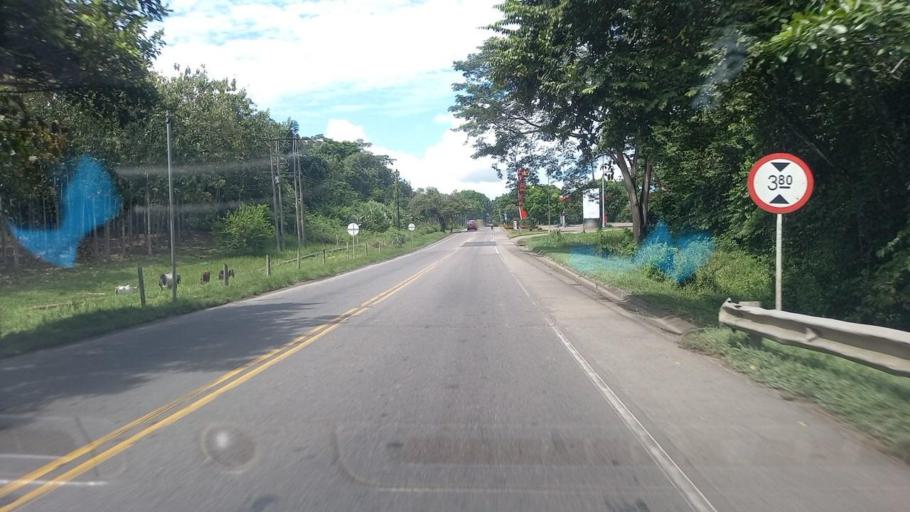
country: CO
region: Santander
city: Sabana de Torres
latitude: 7.1292
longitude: -73.5677
